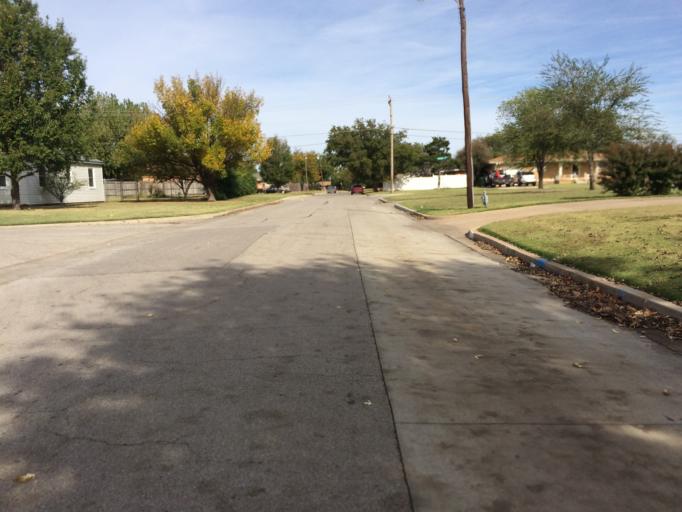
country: US
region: Oklahoma
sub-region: Cleveland County
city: Norman
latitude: 35.2351
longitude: -97.4425
